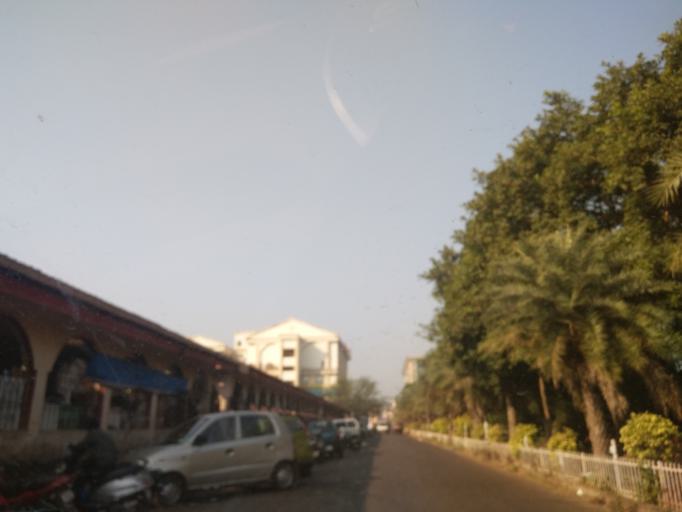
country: IN
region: Goa
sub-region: South Goa
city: Madgaon
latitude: 15.2865
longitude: 73.9584
